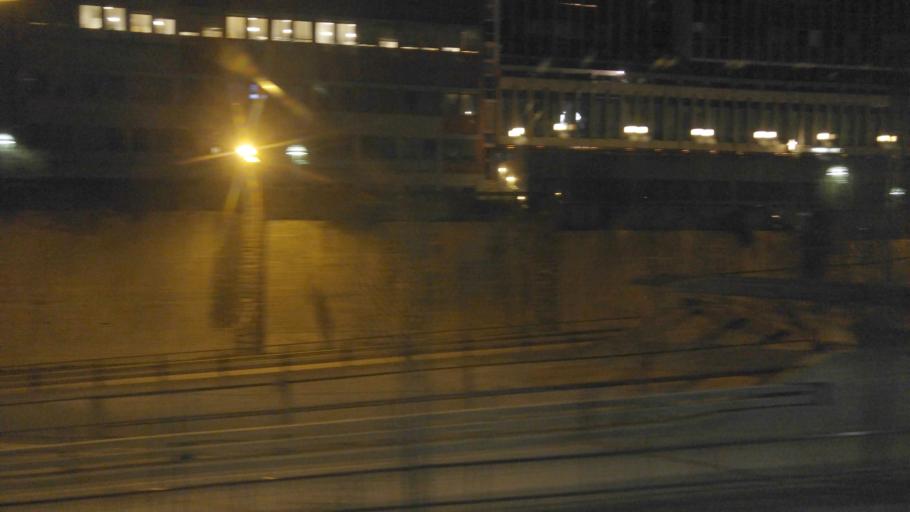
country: NO
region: Oppland
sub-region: Lillehammer
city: Lillehammer
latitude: 61.1163
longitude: 10.4609
